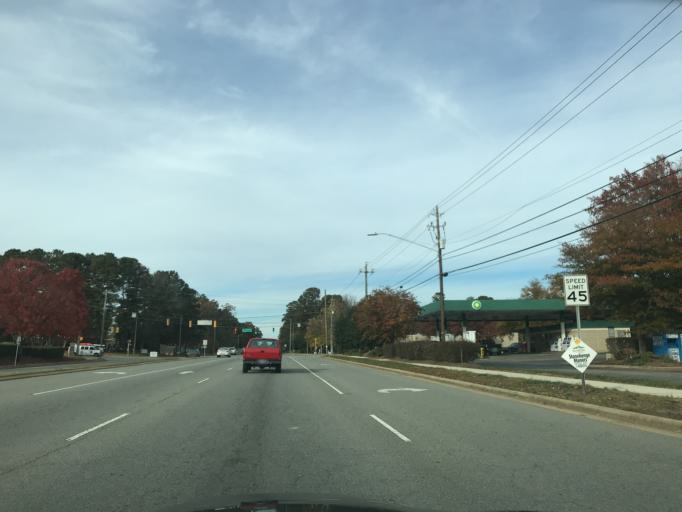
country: US
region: North Carolina
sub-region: Wake County
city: West Raleigh
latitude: 35.8886
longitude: -78.6796
